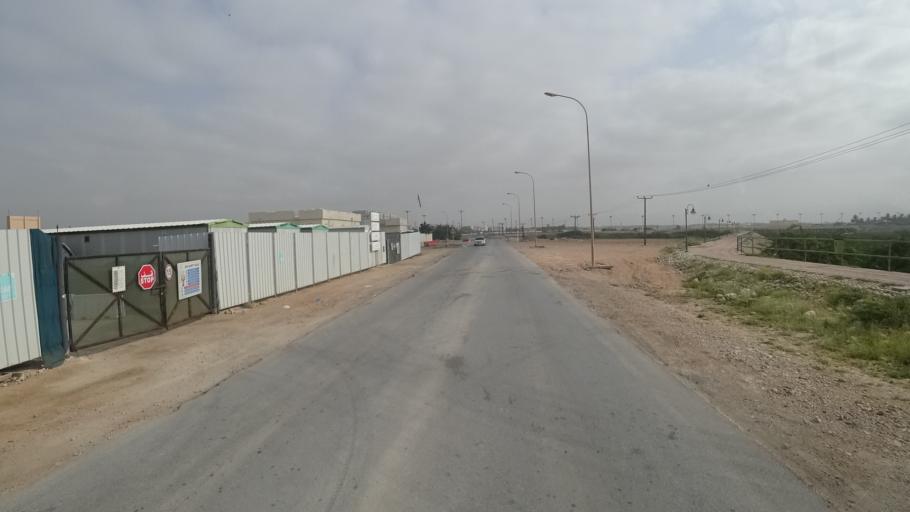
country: OM
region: Zufar
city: Salalah
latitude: 17.0219
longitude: 54.1739
